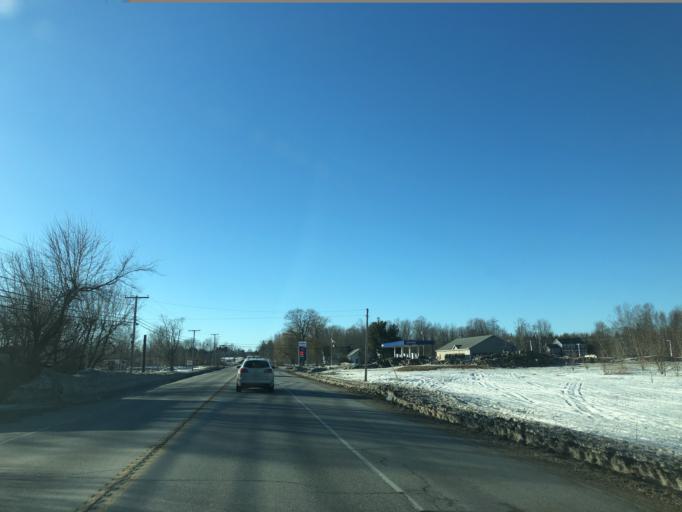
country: US
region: Maine
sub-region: Penobscot County
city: Kenduskeag
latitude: 44.9849
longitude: -69.0054
